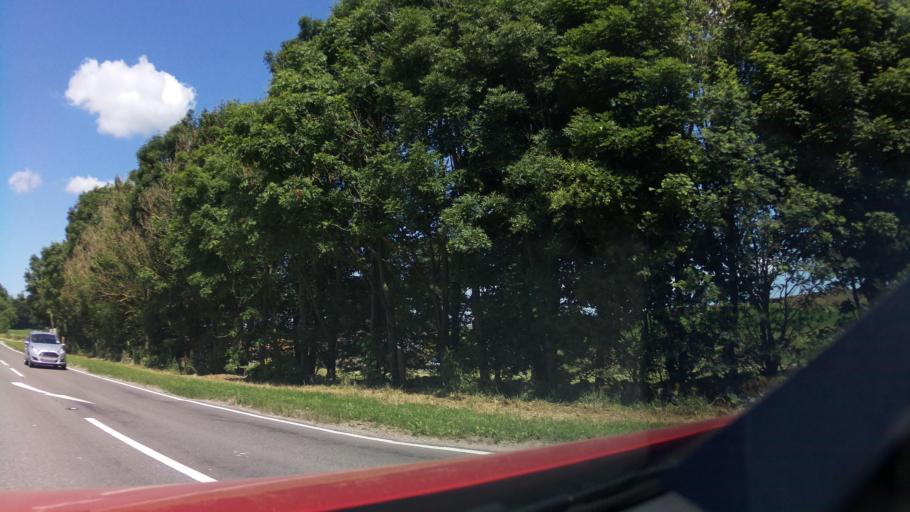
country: GB
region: England
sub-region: Derbyshire
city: Buxton
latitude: 53.2284
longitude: -1.8768
